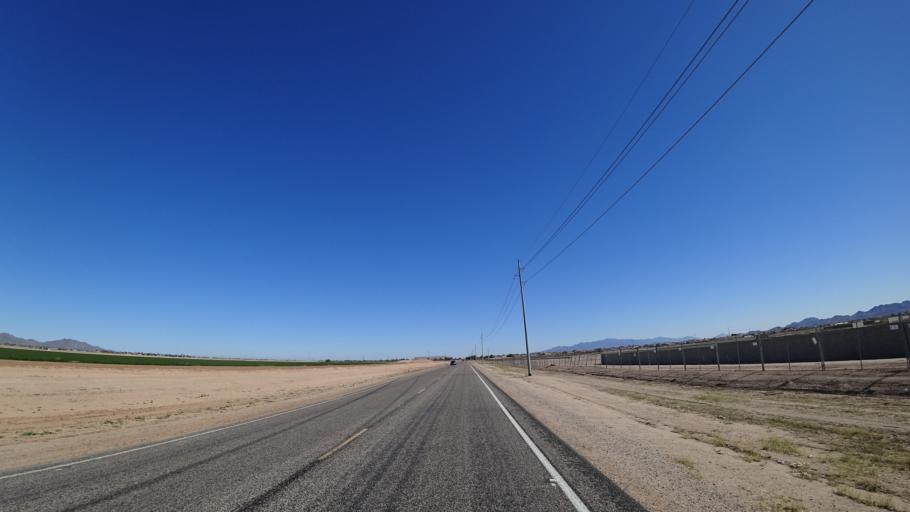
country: US
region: Arizona
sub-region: Maricopa County
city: Buckeye
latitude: 33.3920
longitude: -112.6148
